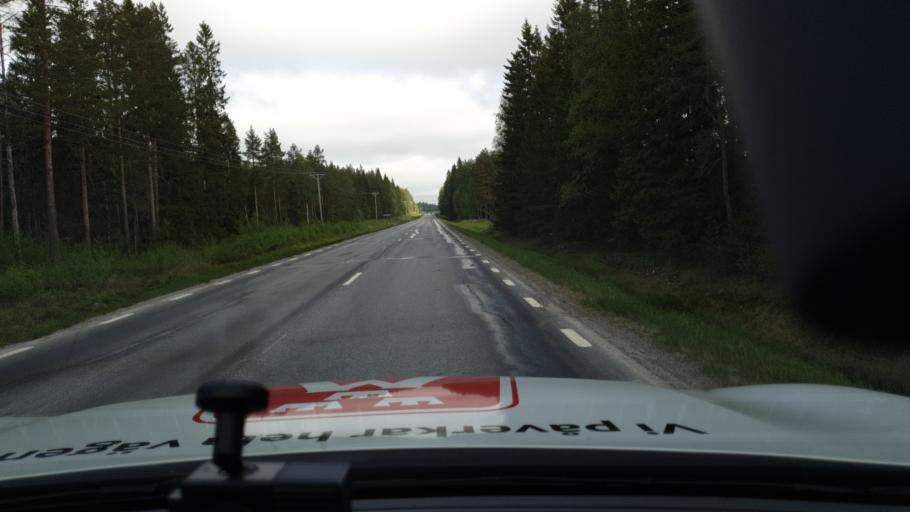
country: SE
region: Vaesterbotten
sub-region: Umea Kommun
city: Roback
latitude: 63.8831
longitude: 20.1992
